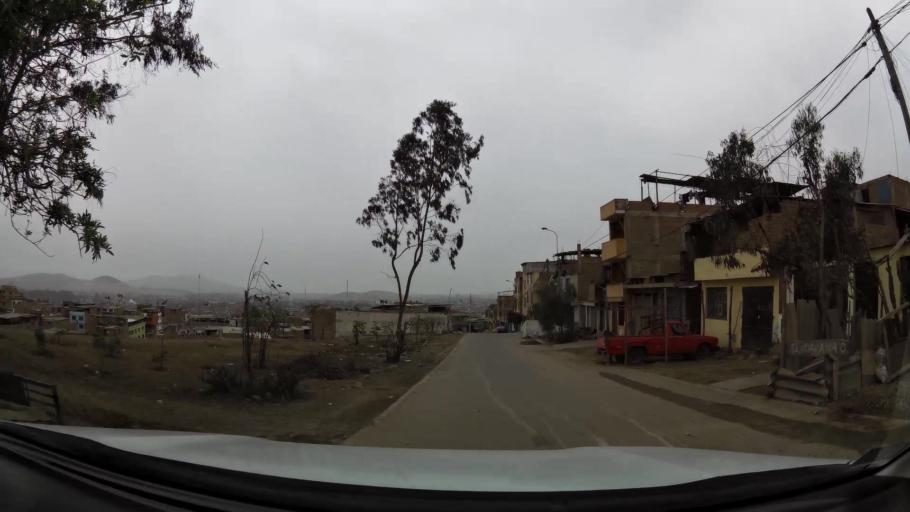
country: PE
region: Lima
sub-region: Lima
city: Surco
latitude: -12.1752
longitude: -76.9606
